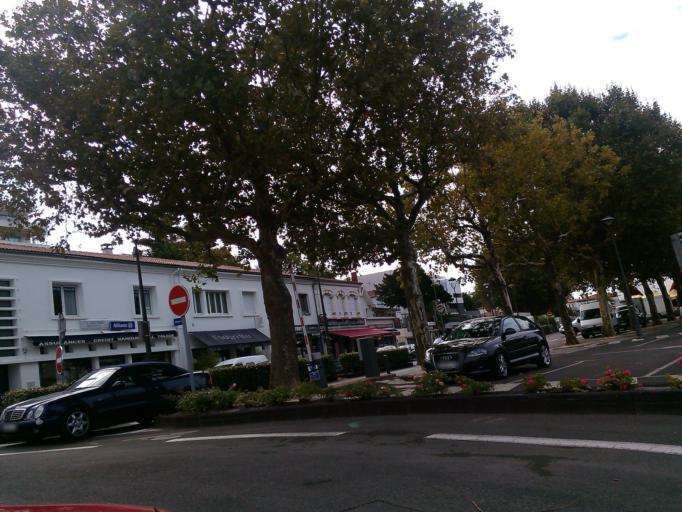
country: FR
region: Poitou-Charentes
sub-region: Departement de la Charente-Maritime
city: Royan
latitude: 45.6286
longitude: -1.0321
